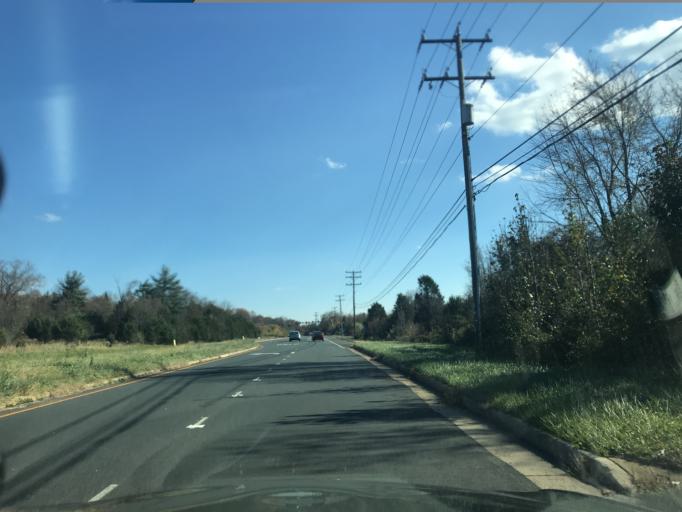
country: US
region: Virginia
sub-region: Fairfax County
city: Floris
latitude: 38.9460
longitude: -77.4257
